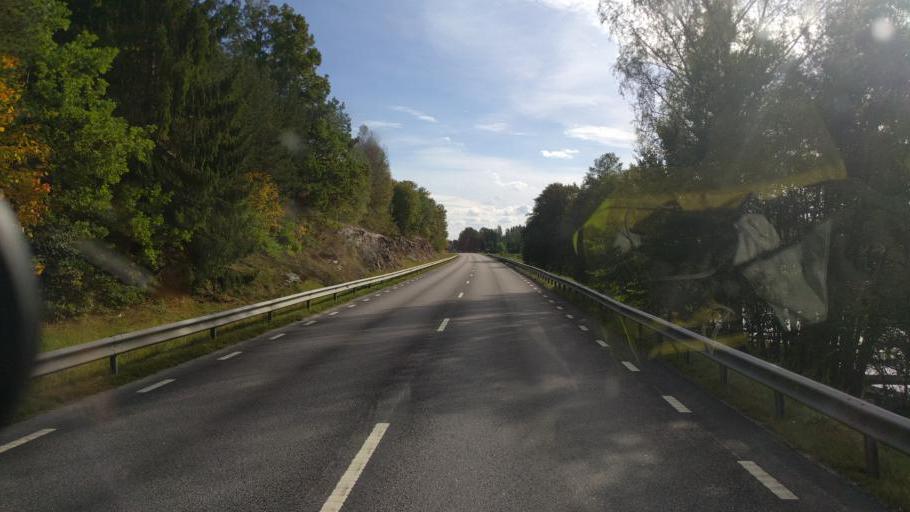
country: SE
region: OEstergoetland
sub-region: Kinda Kommun
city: Kisa
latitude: 57.9328
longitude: 15.6697
